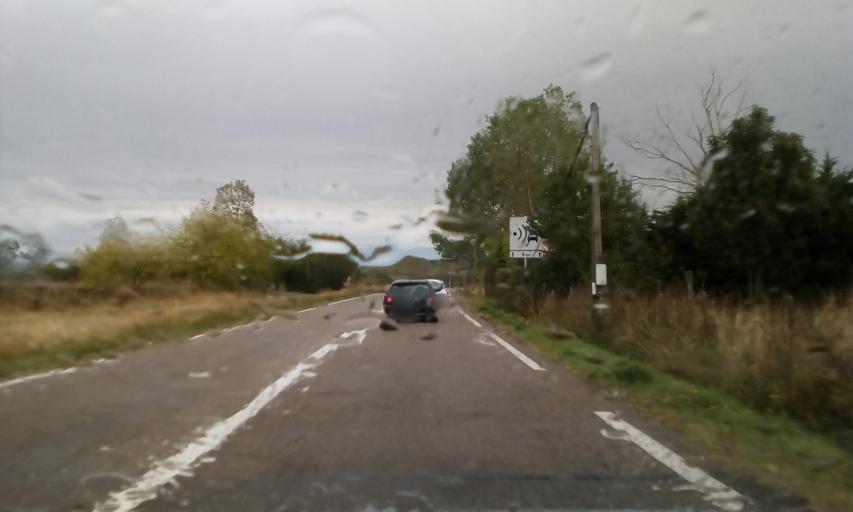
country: FR
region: Rhone-Alpes
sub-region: Departement de l'Ardeche
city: Davezieux
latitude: 45.2440
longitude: 4.7093
